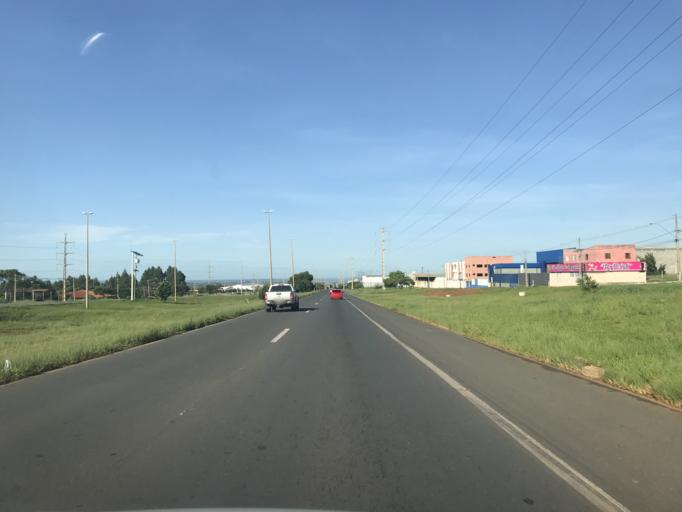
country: BR
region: Federal District
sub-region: Brasilia
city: Brasilia
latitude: -15.8930
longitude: -48.0967
